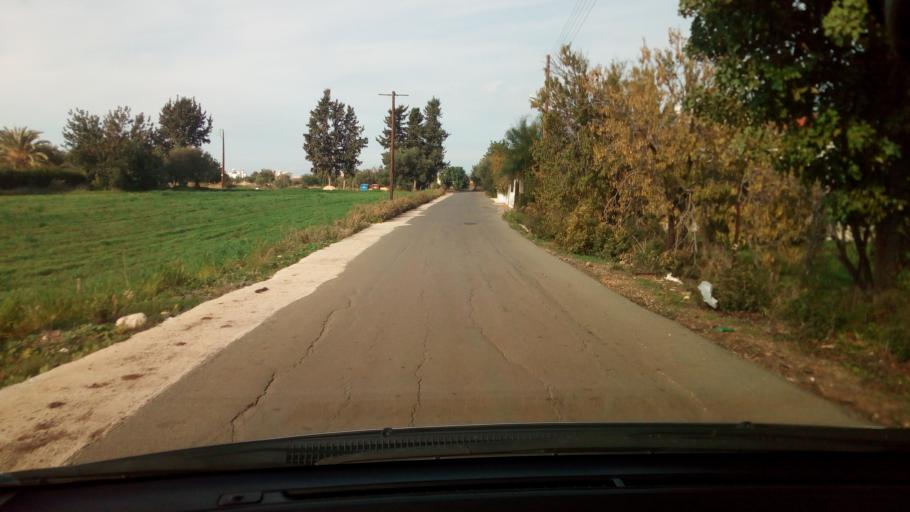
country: CY
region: Pafos
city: Polis
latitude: 35.0369
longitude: 32.3771
